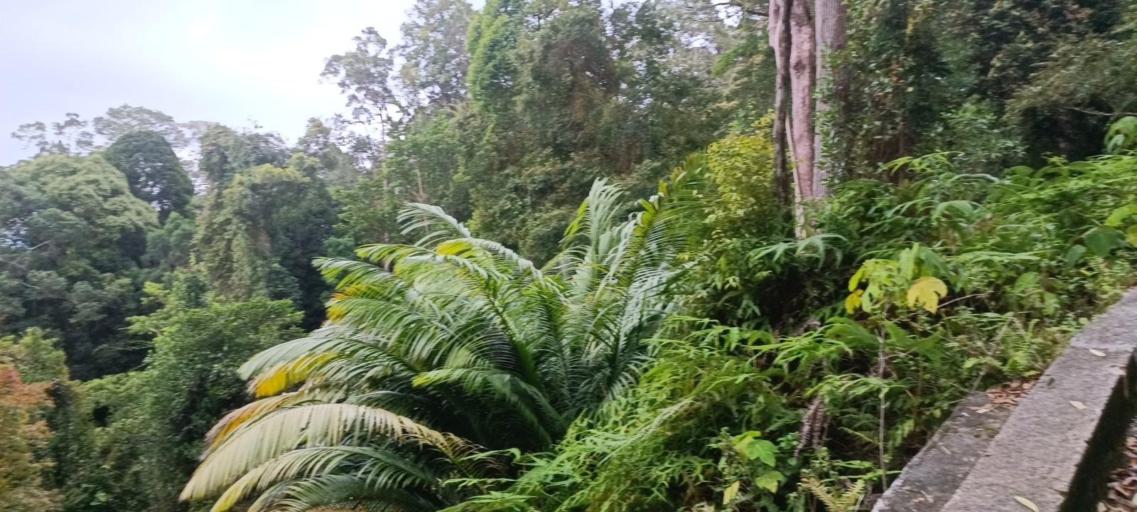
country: MY
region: Perak
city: Taiping
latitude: 4.8658
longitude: 100.7696
